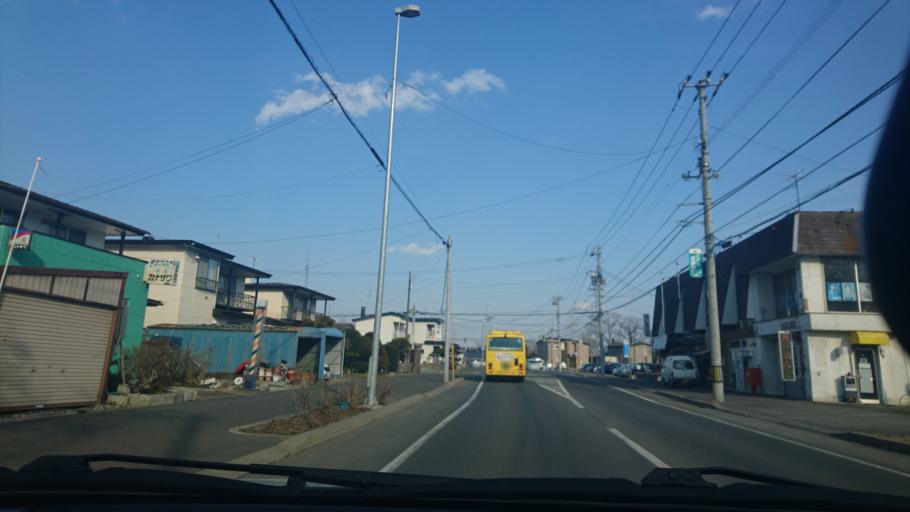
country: JP
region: Hokkaido
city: Obihiro
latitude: 42.9240
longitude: 143.1763
